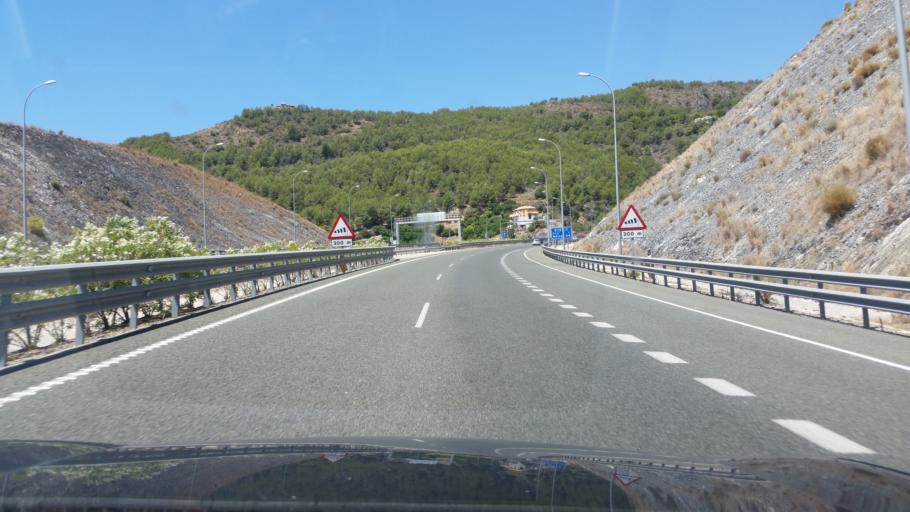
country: ES
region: Andalusia
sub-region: Provincia de Granada
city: La Herradura
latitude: 36.7496
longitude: -3.7576
